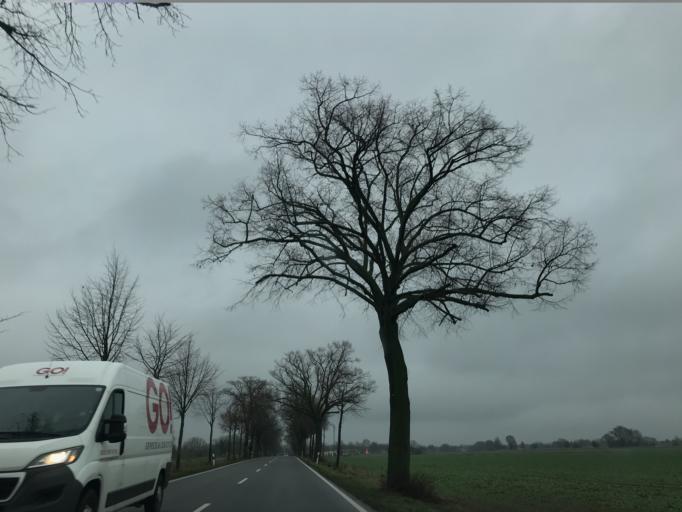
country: DE
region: Brandenburg
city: Kremmen
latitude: 52.7542
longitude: 13.0154
